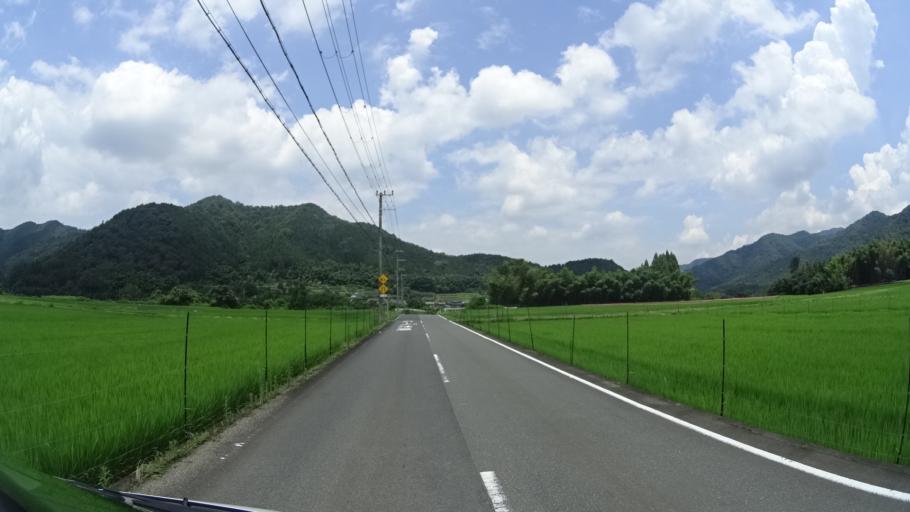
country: JP
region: Kyoto
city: Ayabe
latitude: 35.2004
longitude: 135.2442
